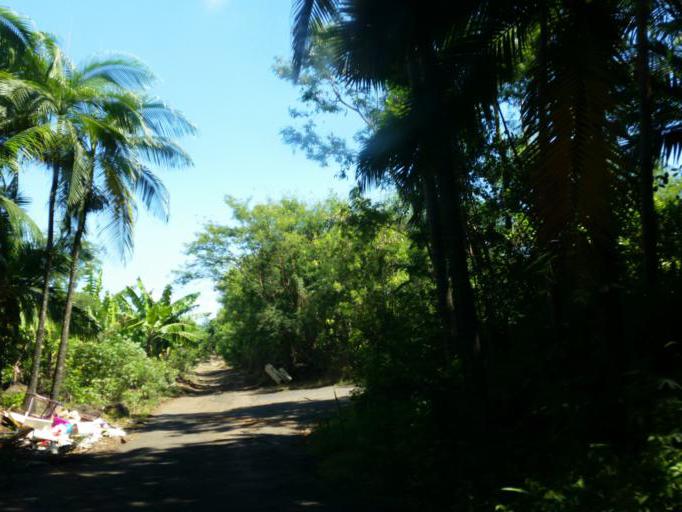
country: RE
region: Reunion
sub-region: Reunion
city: Sainte-Marie
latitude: -20.9060
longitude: 55.5150
